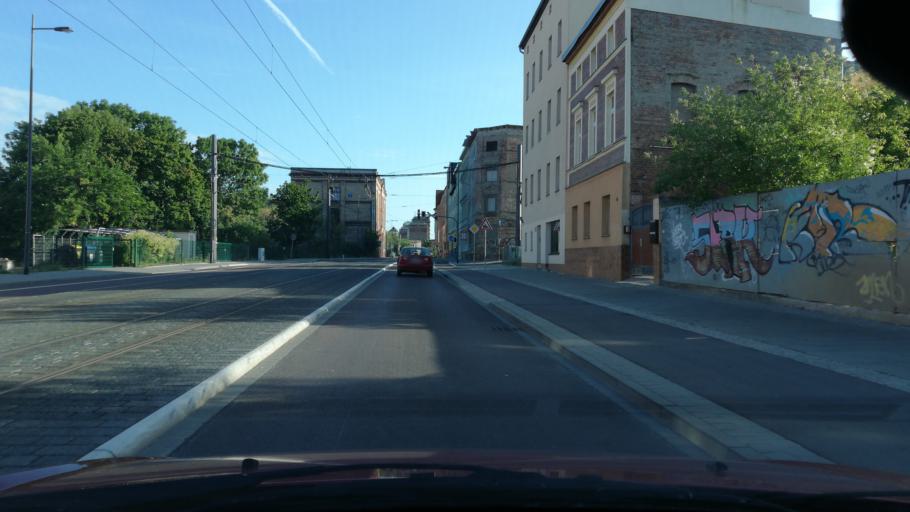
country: DE
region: Saxony-Anhalt
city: Halle Neustadt
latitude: 51.4717
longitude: 11.9594
